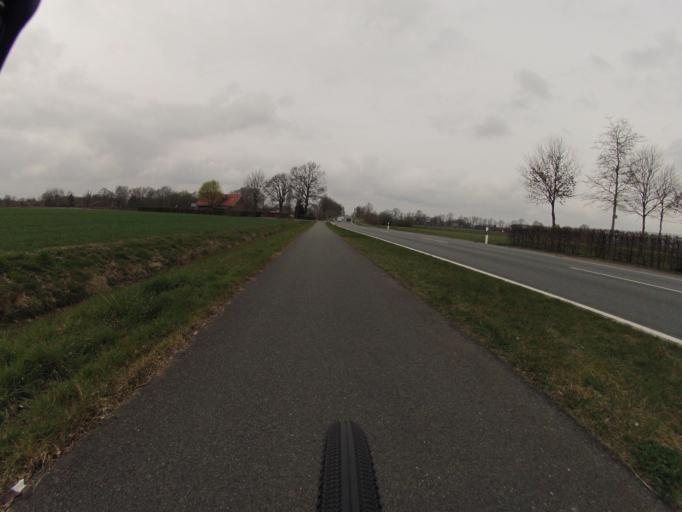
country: DE
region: North Rhine-Westphalia
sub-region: Regierungsbezirk Munster
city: Recke
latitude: 52.3535
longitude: 7.7258
